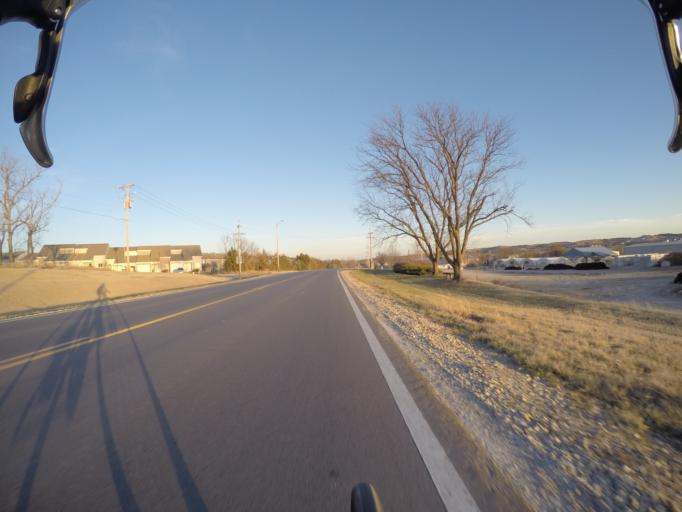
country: US
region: Kansas
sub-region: Riley County
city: Manhattan
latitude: 39.1946
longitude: -96.6454
